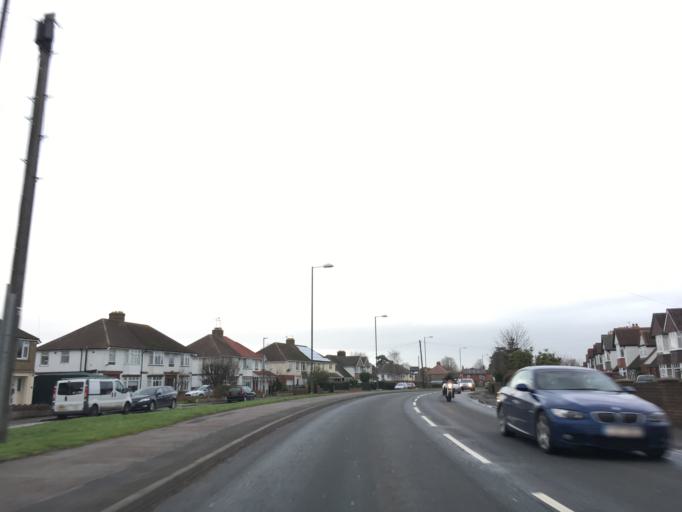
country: GB
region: England
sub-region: Gloucestershire
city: Barnwood
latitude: 51.8835
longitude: -2.1931
